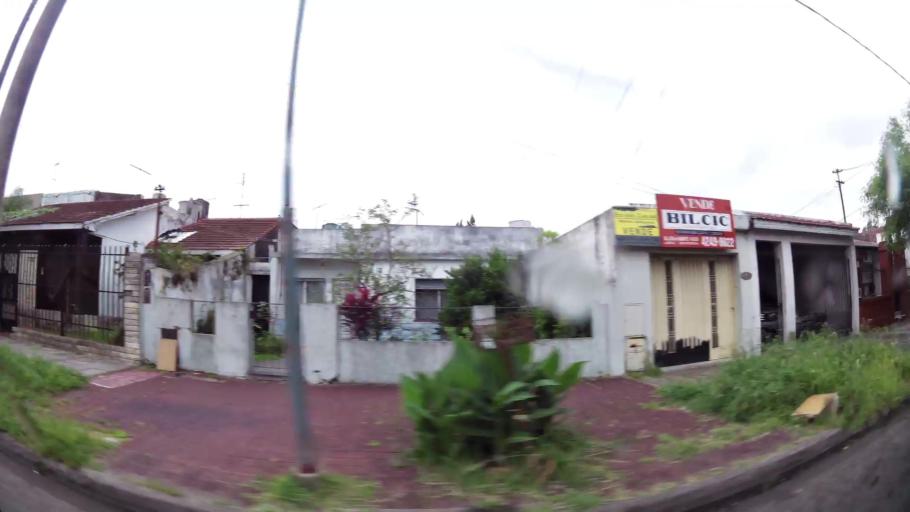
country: AR
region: Buenos Aires
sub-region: Partido de Lanus
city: Lanus
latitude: -34.6972
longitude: -58.4029
